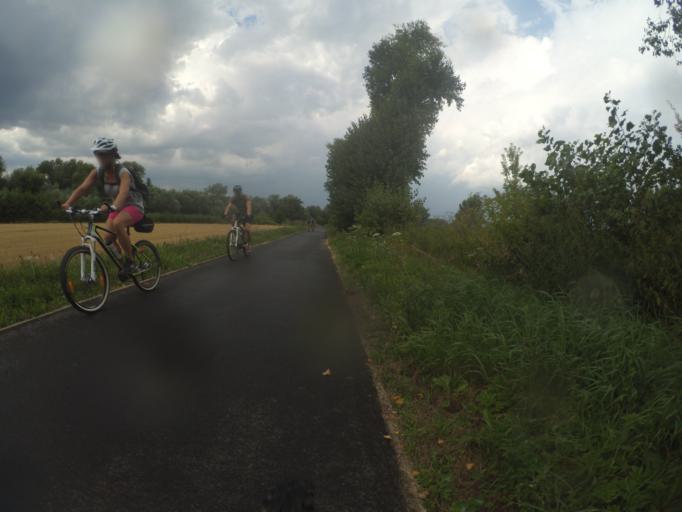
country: CZ
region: Central Bohemia
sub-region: Okres Melnik
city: Melnik
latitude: 50.3646
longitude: 14.4549
